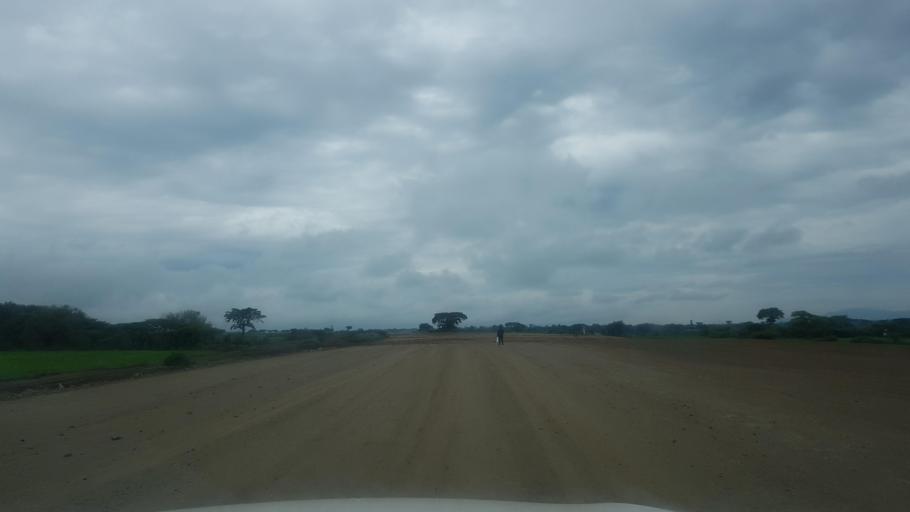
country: ET
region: Oromiya
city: Shashemene
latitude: 7.3818
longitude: 38.6481
